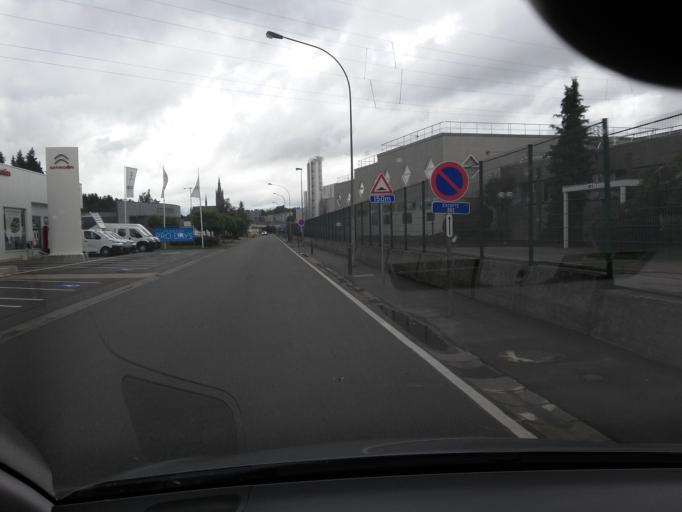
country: BE
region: Wallonia
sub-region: Province du Luxembourg
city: Arlon
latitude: 49.6737
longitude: 5.8203
